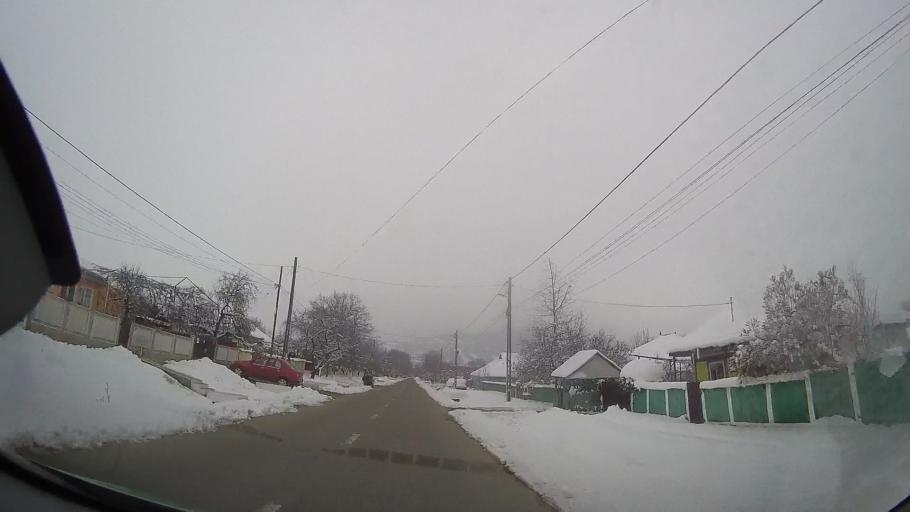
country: RO
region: Vaslui
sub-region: Comuna Bacesti
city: Bacesti
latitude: 46.8220
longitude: 27.2018
